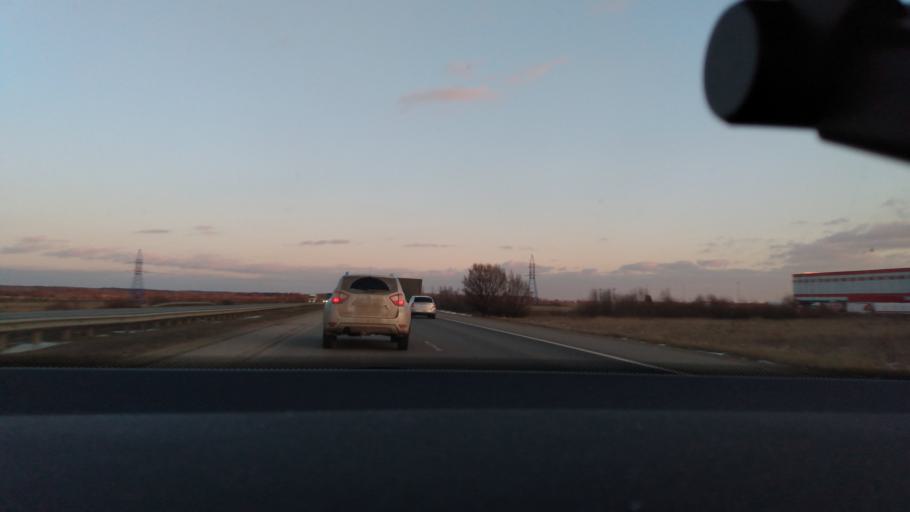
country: RU
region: Moskovskaya
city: Kolomna
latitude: 55.1171
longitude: 38.8373
